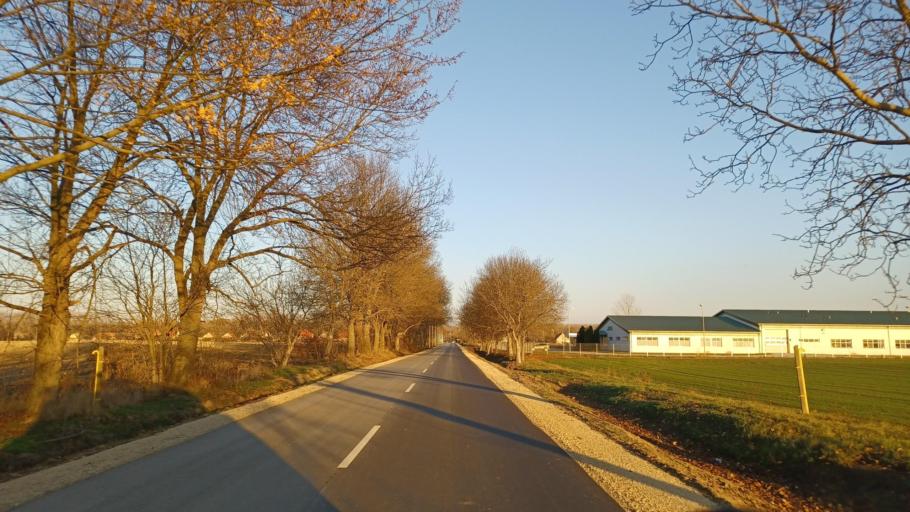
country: HU
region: Bacs-Kiskun
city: Batya
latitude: 46.4875
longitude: 18.8920
